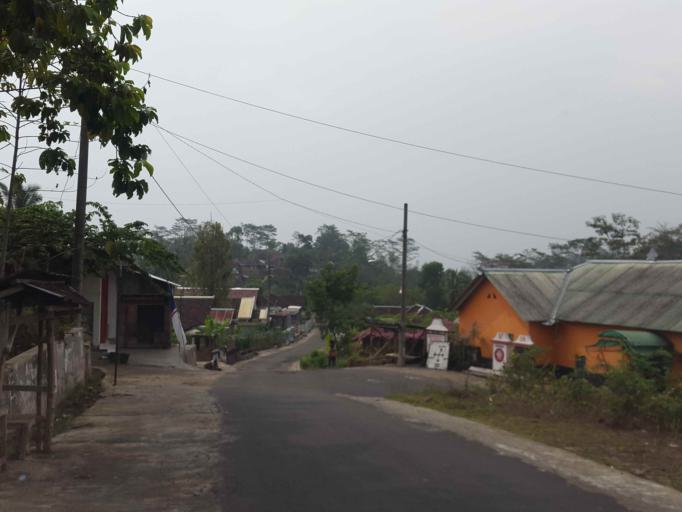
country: ID
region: Central Java
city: Jatiroto
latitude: -7.6886
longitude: 111.0968
